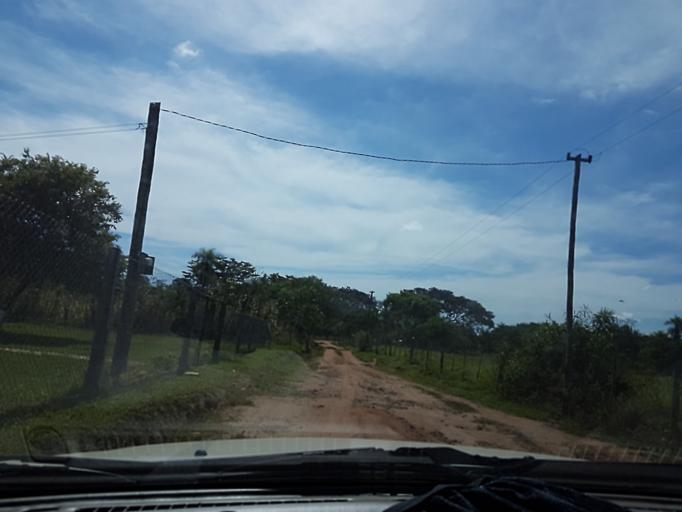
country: PY
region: Cordillera
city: Arroyos y Esteros
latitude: -24.9786
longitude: -57.1957
